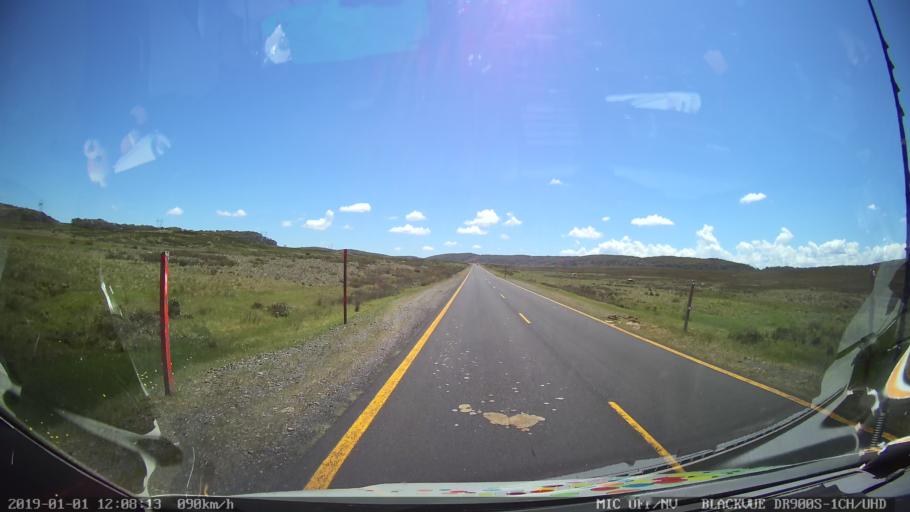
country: AU
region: New South Wales
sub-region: Tumut Shire
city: Tumut
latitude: -35.8232
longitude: 148.4936
